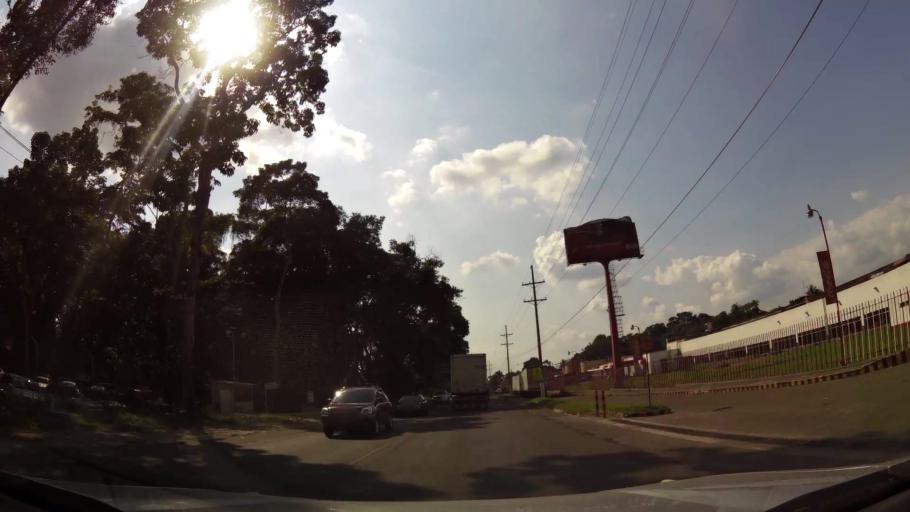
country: GT
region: Retalhuleu
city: San Sebastian
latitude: 14.5748
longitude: -91.6432
